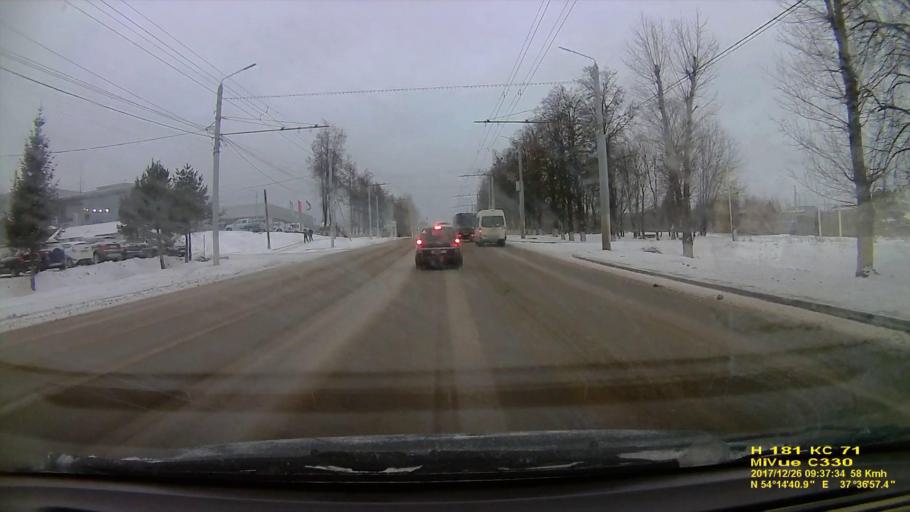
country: RU
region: Tula
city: Gorelki
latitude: 54.2447
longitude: 37.6159
